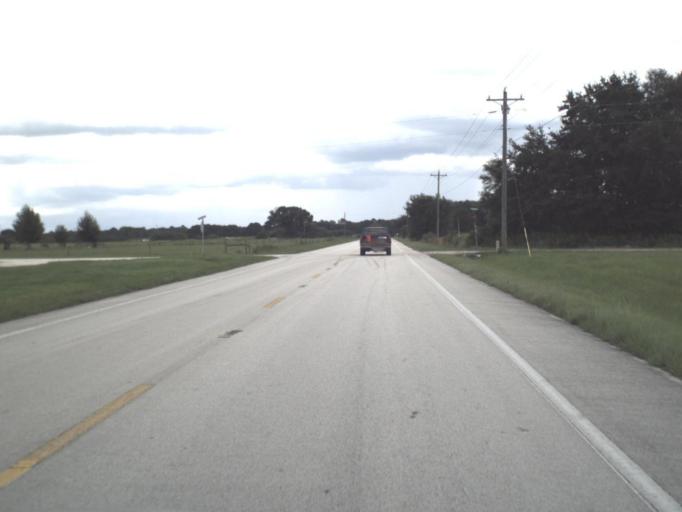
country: US
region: Florida
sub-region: Hardee County
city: Zolfo Springs
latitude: 27.5444
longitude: -81.7199
